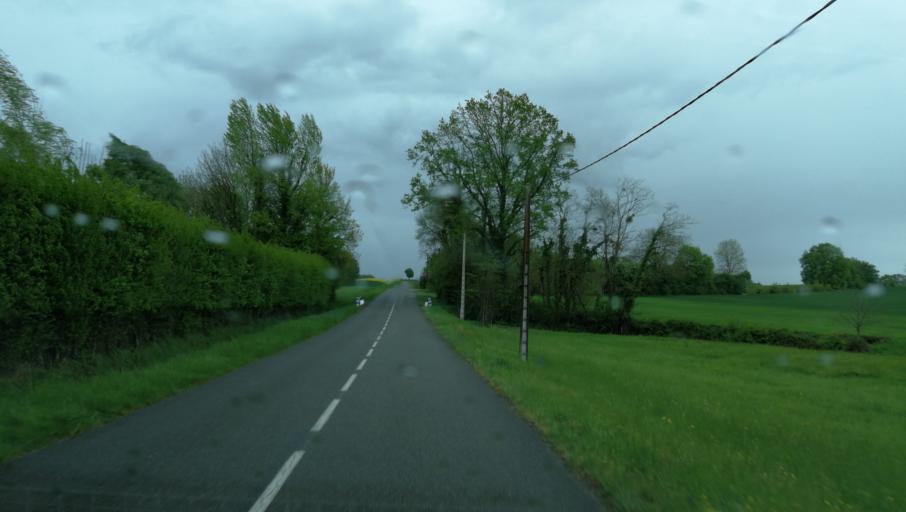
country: FR
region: Franche-Comte
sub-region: Departement du Jura
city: Bletterans
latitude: 46.7788
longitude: 5.4206
